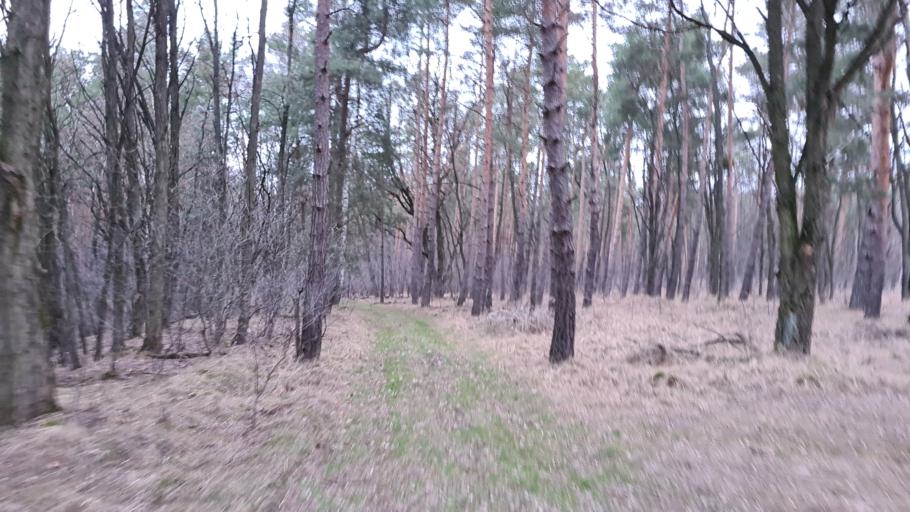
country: DE
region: Brandenburg
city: Trobitz
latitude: 51.5855
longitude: 13.4561
